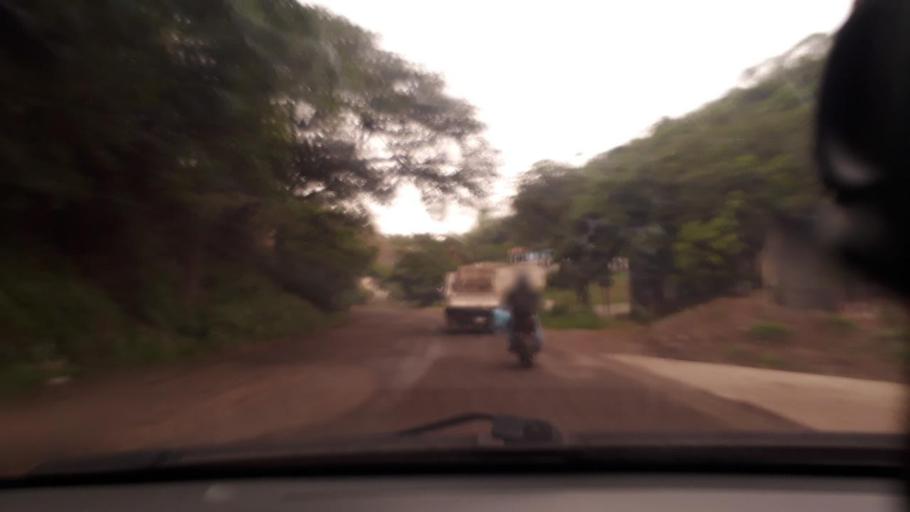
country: GT
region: Jutiapa
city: Asuncion Mita
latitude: 14.2731
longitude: -89.7283
